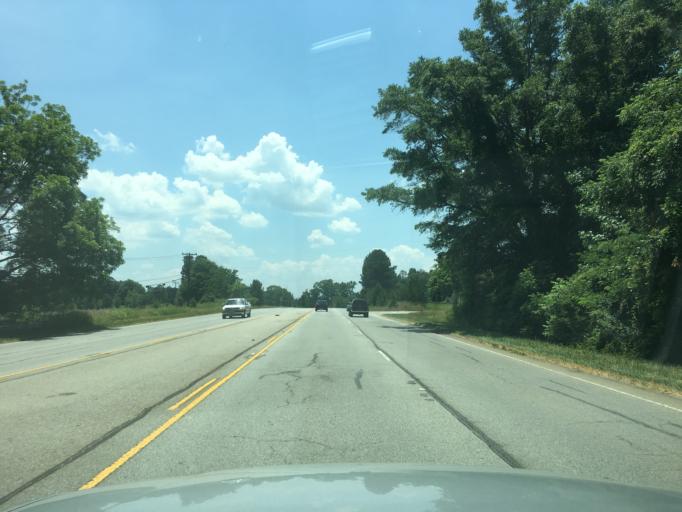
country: US
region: South Carolina
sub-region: Anderson County
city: Northlake
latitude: 34.6069
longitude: -82.6112
